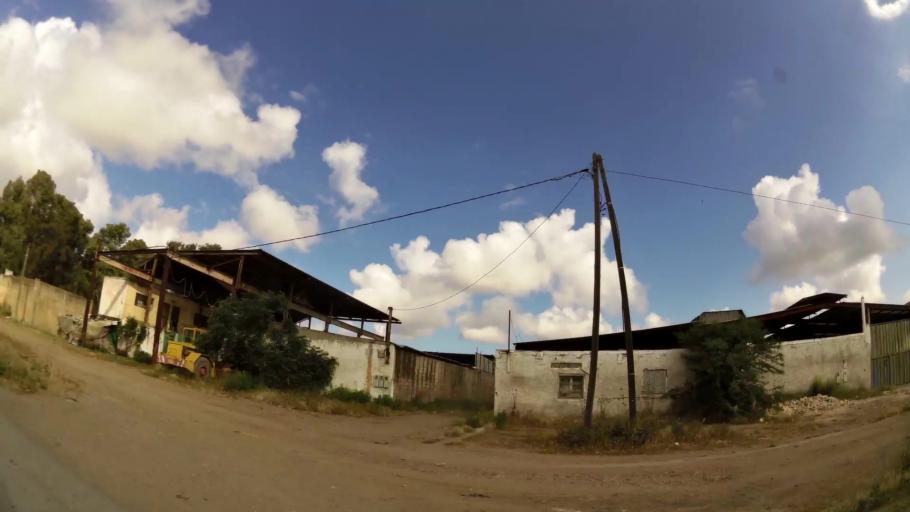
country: MA
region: Gharb-Chrarda-Beni Hssen
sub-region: Kenitra Province
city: Kenitra
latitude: 34.2691
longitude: -6.5681
